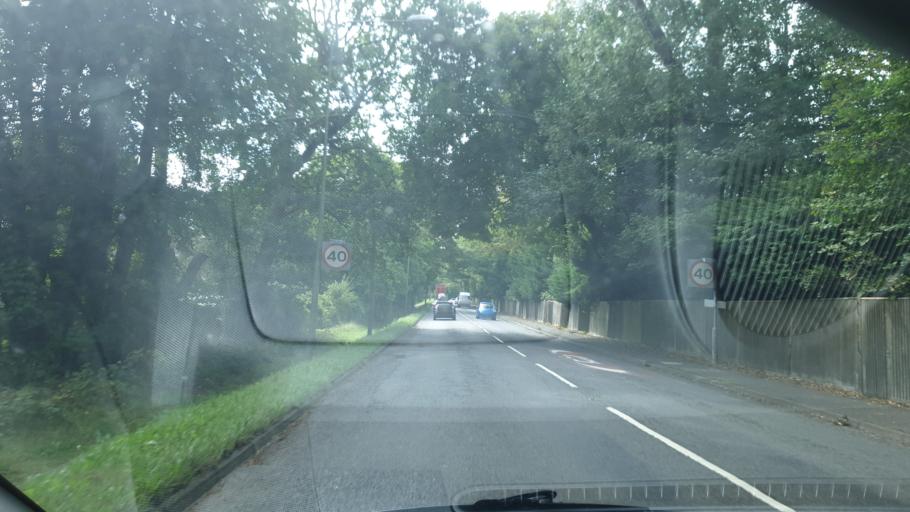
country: GB
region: England
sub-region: East Sussex
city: Forest Row
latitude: 51.0939
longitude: 0.0331
